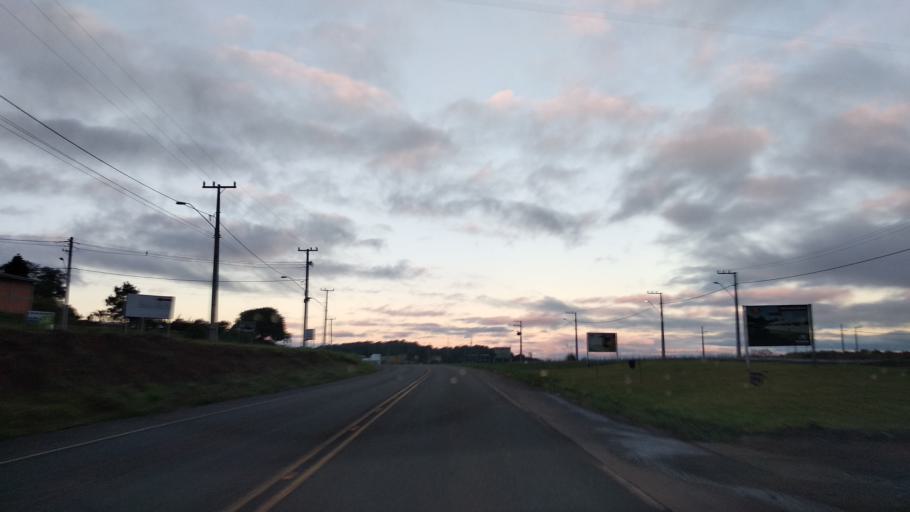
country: BR
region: Santa Catarina
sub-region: Campos Novos
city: Campos Novos
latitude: -27.3775
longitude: -51.2067
